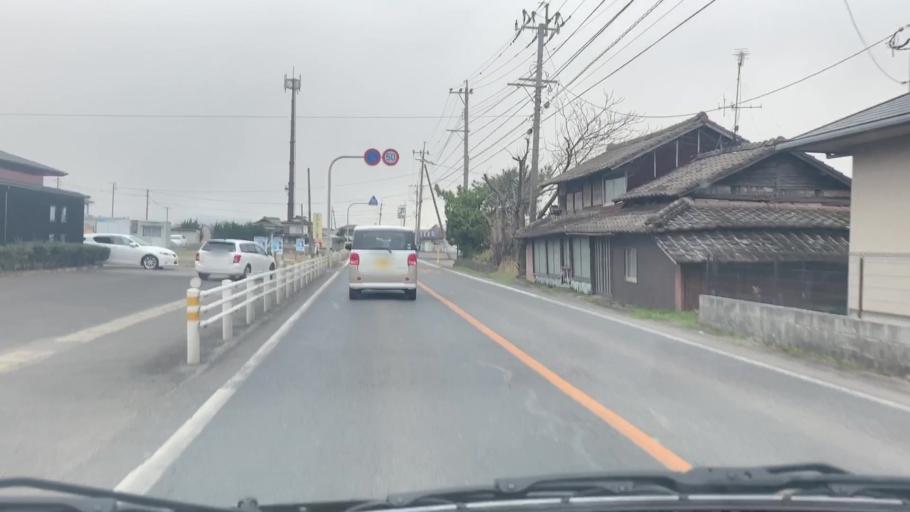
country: JP
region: Saga Prefecture
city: Saga-shi
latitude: 33.1859
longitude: 130.1925
